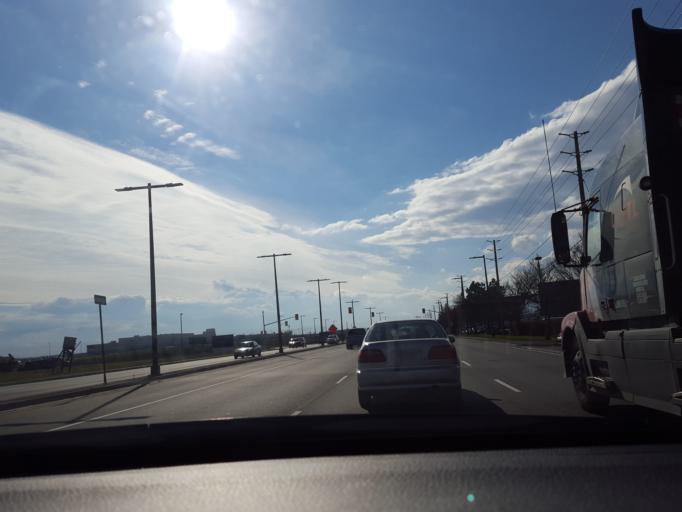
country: CA
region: Ontario
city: Etobicoke
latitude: 43.6923
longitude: -79.6554
